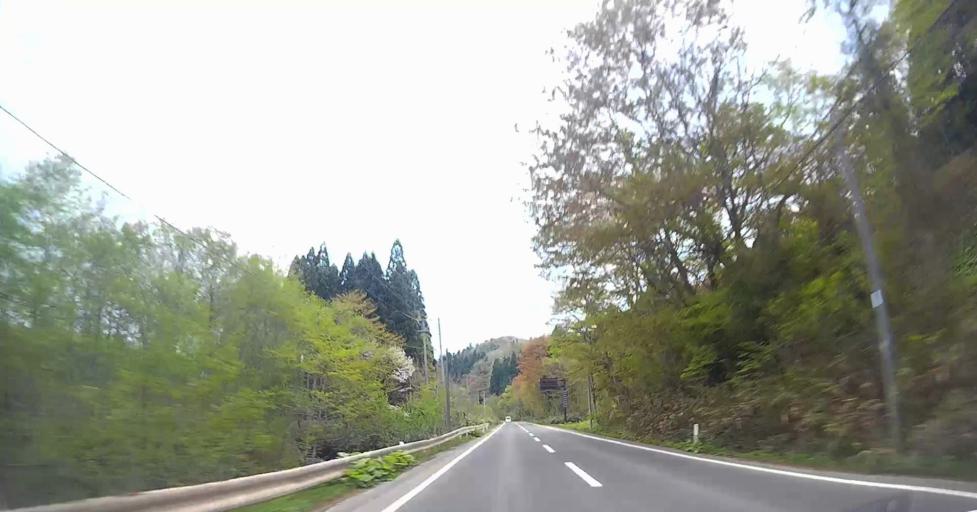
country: JP
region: Aomori
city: Goshogawara
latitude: 41.1277
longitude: 140.5198
